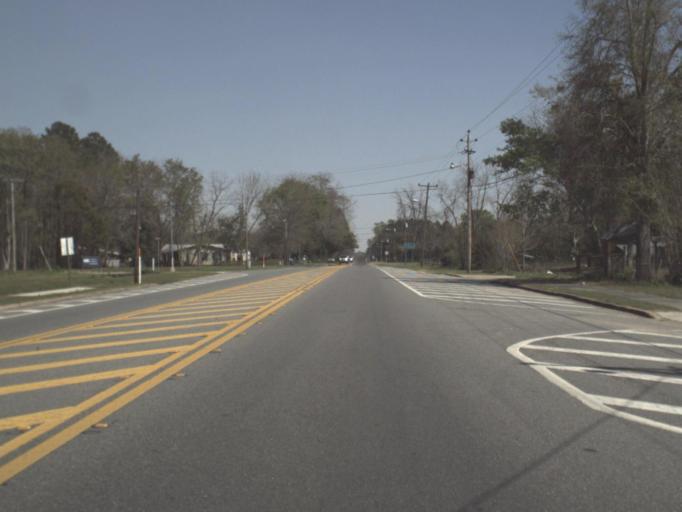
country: US
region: Florida
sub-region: Liberty County
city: Bristol
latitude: 30.4319
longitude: -84.9704
